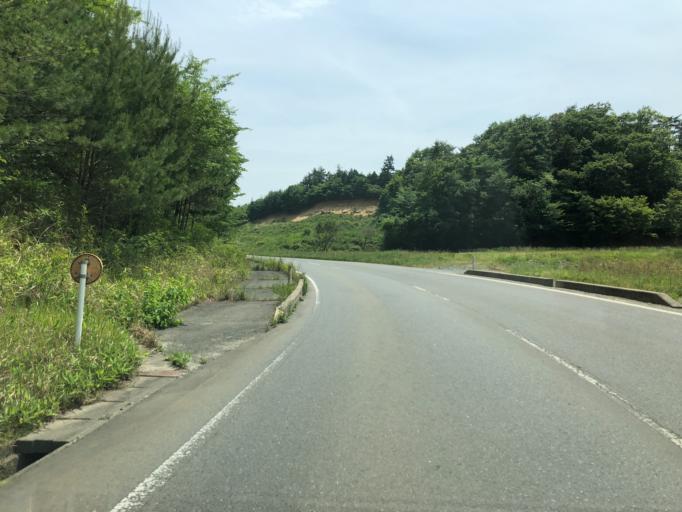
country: JP
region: Fukushima
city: Namie
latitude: 37.5568
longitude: 140.9267
